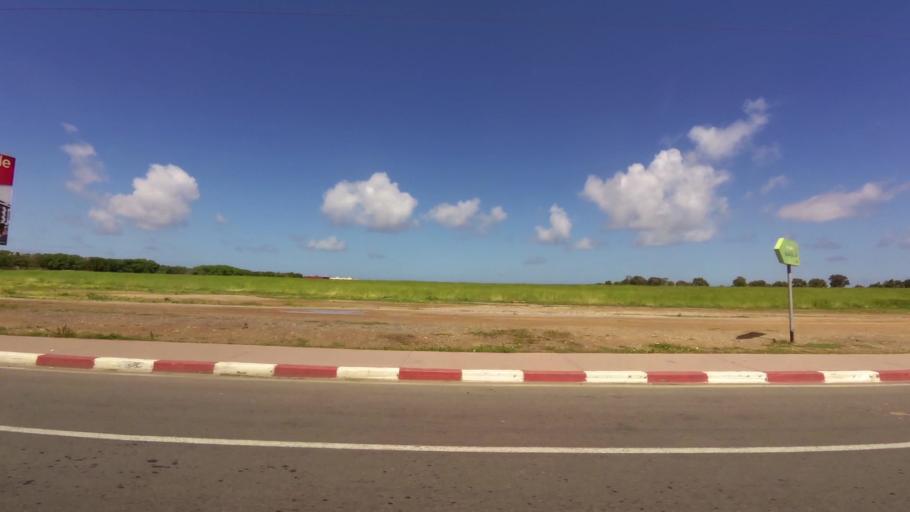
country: MA
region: Grand Casablanca
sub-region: Nouaceur
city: Dar Bouazza
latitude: 33.5385
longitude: -7.7179
